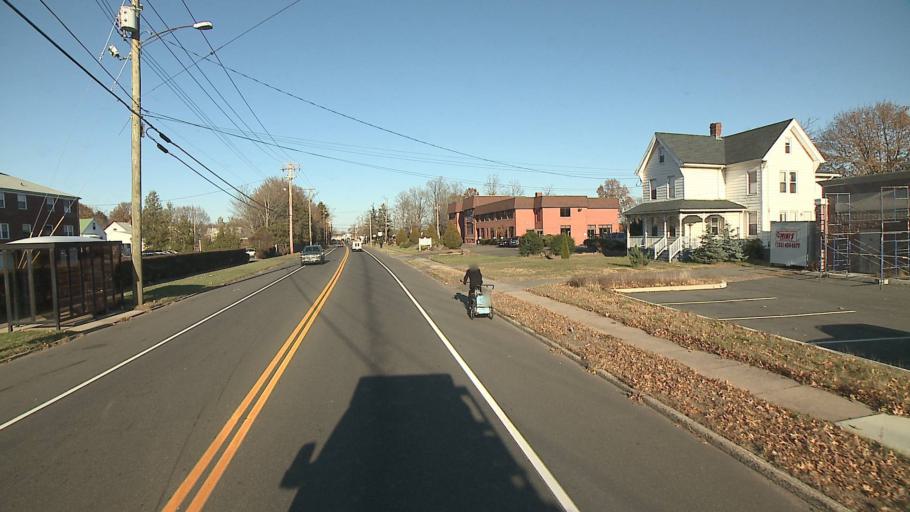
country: US
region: Connecticut
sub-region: New Haven County
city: New Haven
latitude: 41.3380
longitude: -72.8979
